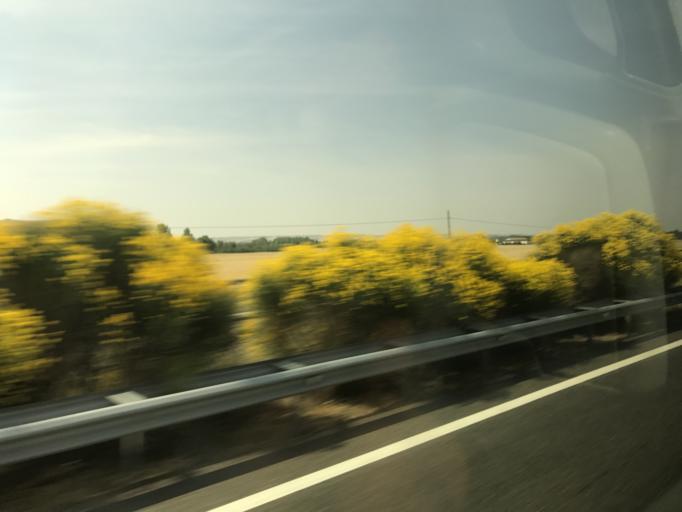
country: ES
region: Castille and Leon
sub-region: Provincia de Palencia
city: Palenzuela
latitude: 42.1239
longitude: -4.1424
